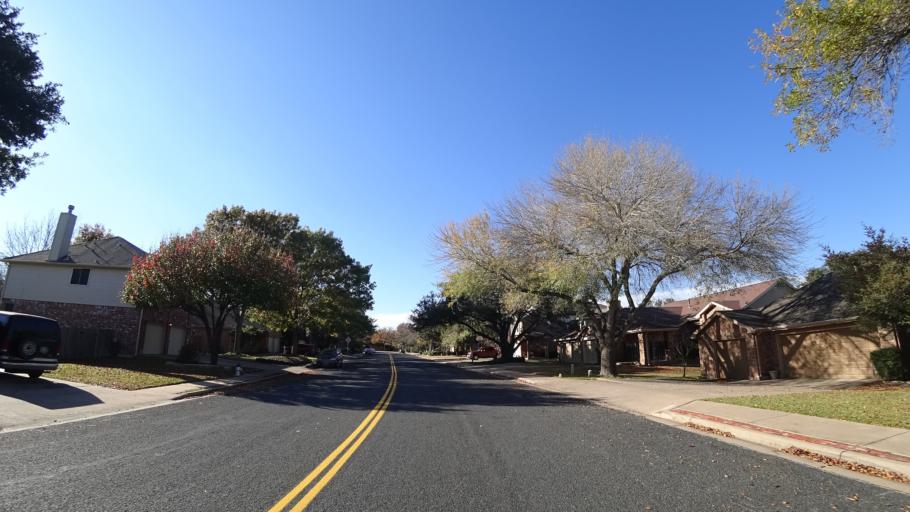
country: US
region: Texas
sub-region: Williamson County
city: Brushy Creek
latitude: 30.4896
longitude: -97.7411
